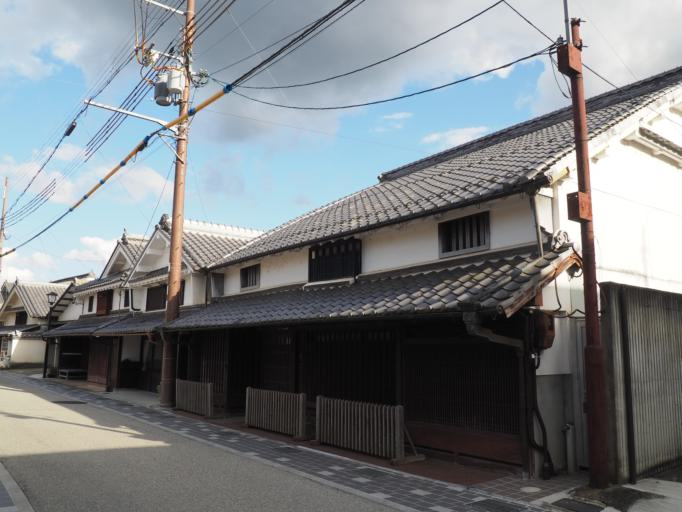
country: JP
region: Hyogo
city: Sasayama
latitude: 35.0717
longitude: 135.2252
